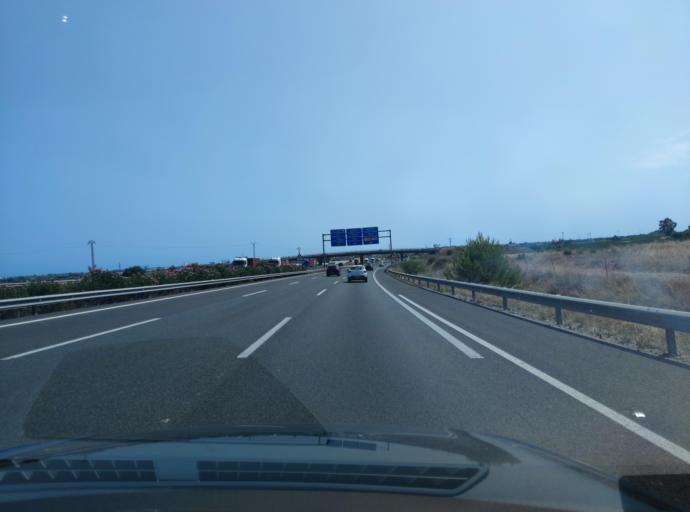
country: ES
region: Valencia
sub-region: Provincia de Valencia
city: Pucol
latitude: 39.6449
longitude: -0.3003
